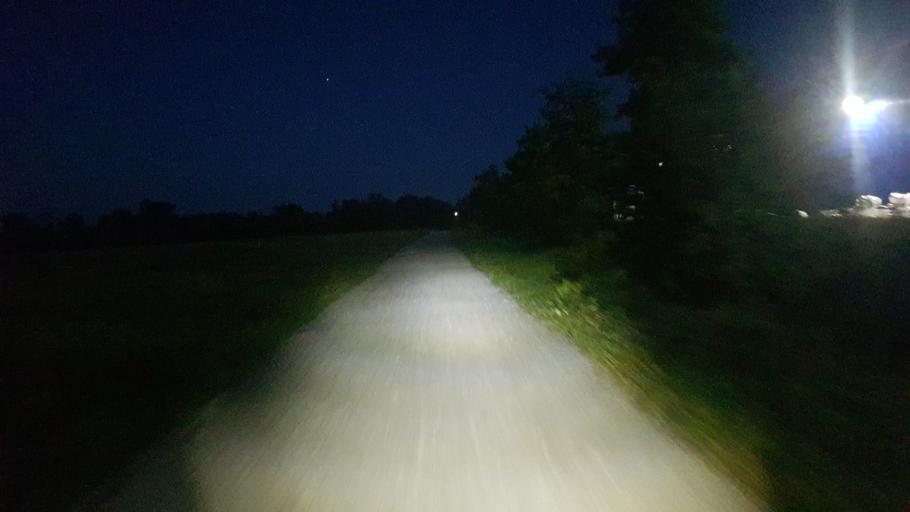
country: DE
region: Bavaria
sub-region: Upper Bavaria
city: Pasing
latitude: 48.1402
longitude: 11.4345
